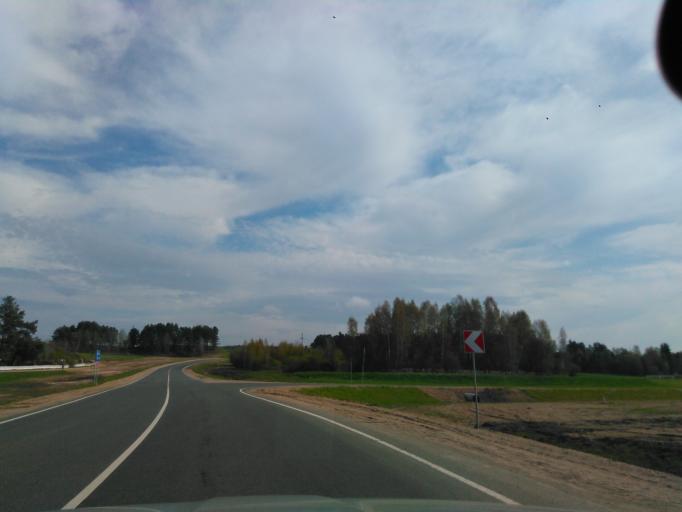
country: BY
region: Minsk
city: Rakaw
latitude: 53.9670
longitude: 27.0742
